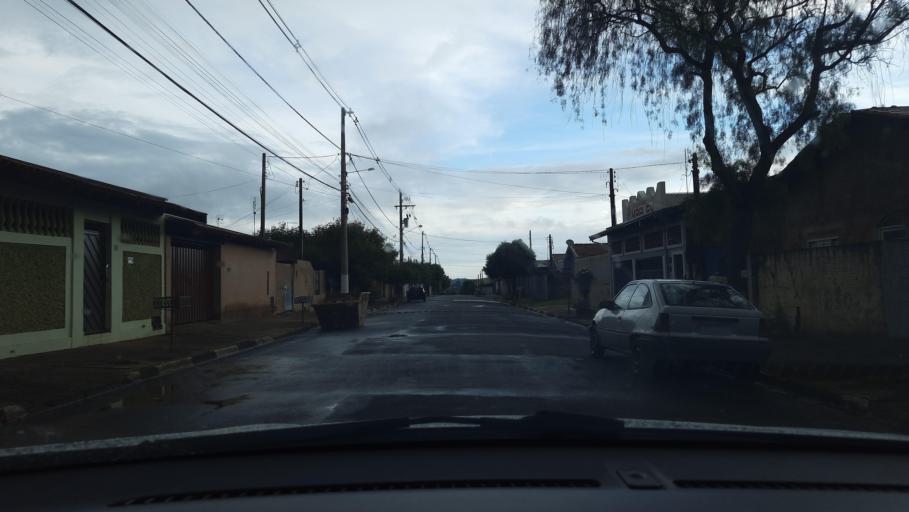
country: BR
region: Sao Paulo
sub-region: Casa Branca
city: Casa Branca
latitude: -21.7578
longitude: -47.0767
